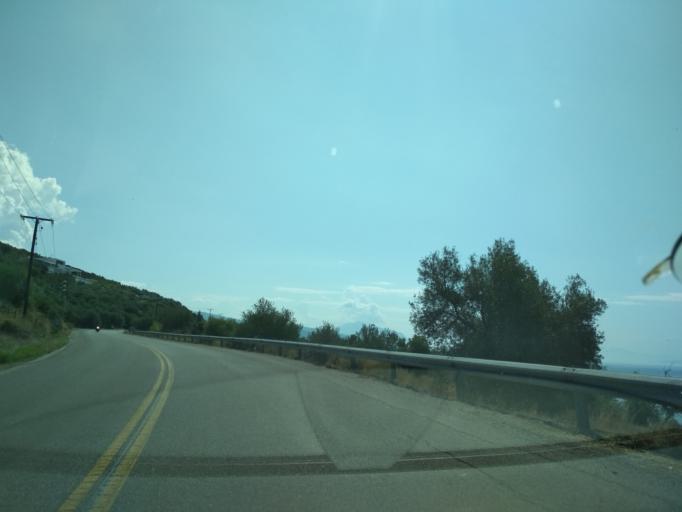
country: GR
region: Central Greece
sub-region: Nomos Evvoias
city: Roviai
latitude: 38.8395
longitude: 23.1758
